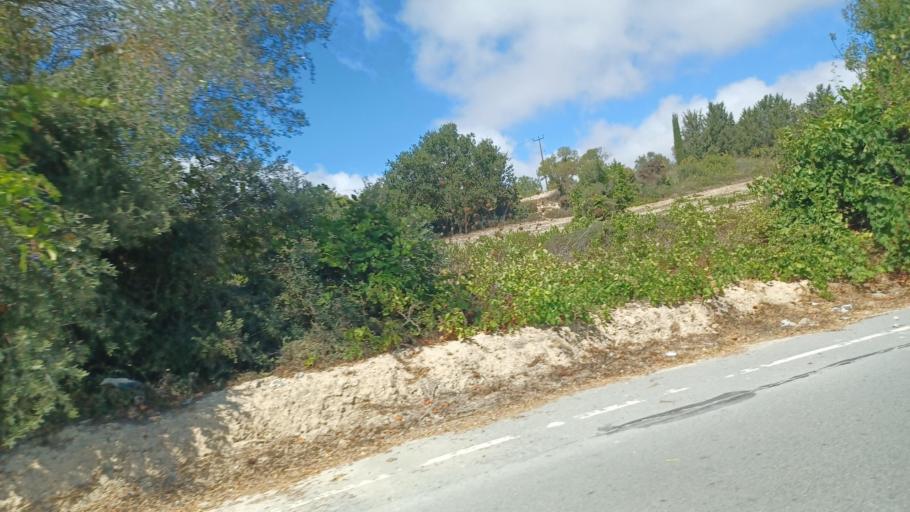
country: CY
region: Pafos
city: Tala
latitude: 34.8475
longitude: 32.4629
